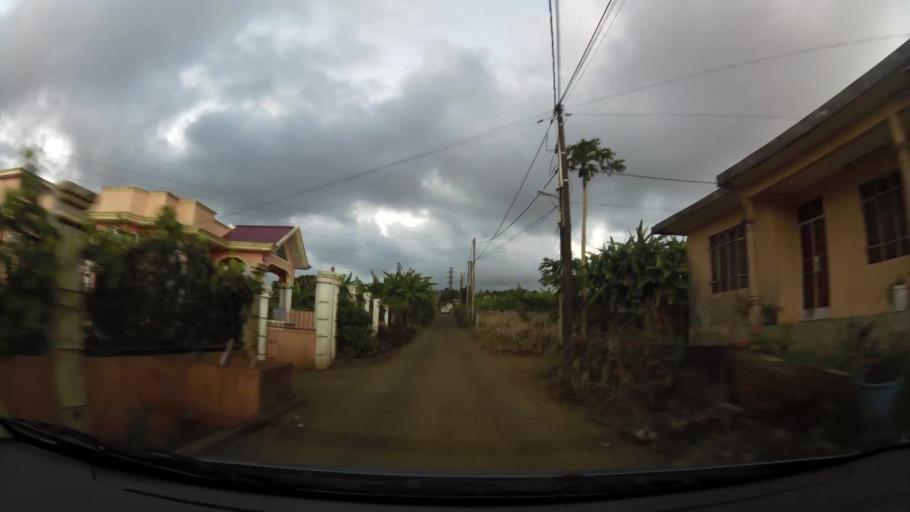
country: MU
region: Plaines Wilhems
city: Curepipe
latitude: -20.2994
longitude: 57.5332
